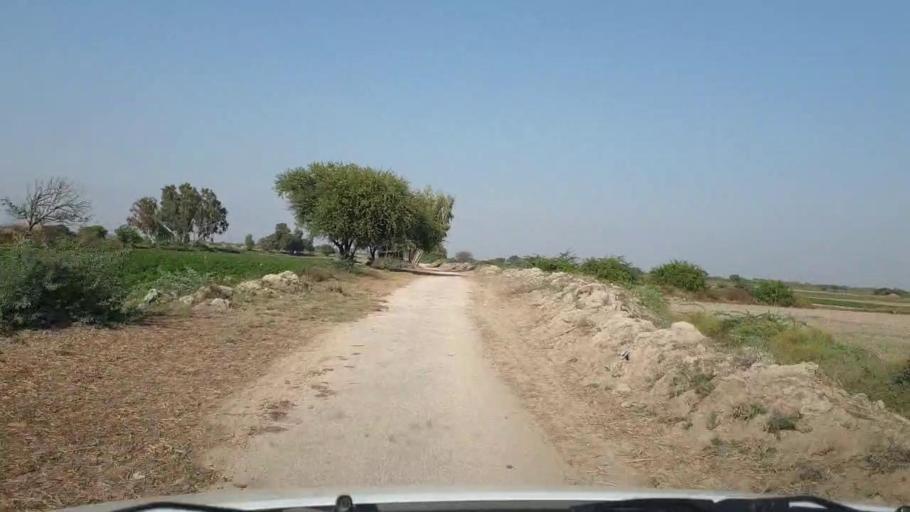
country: PK
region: Sindh
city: Mirpur Sakro
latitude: 24.5952
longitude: 67.6297
